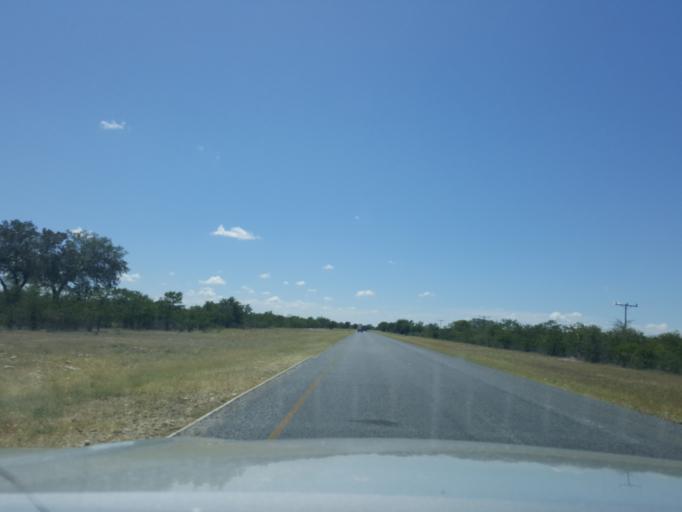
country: BW
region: Central
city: Gweta
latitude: -20.1841
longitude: 25.3004
